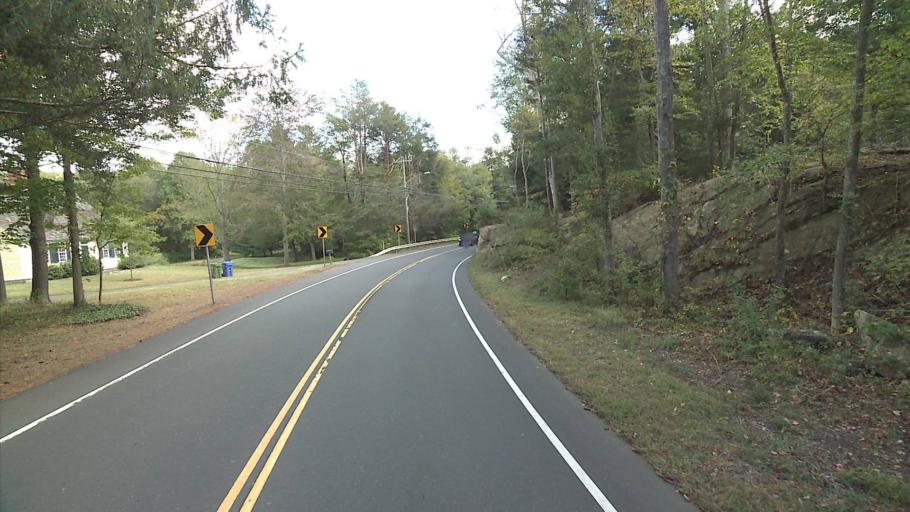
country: US
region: Connecticut
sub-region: Middlesex County
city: Chester Center
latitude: 41.4009
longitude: -72.4922
